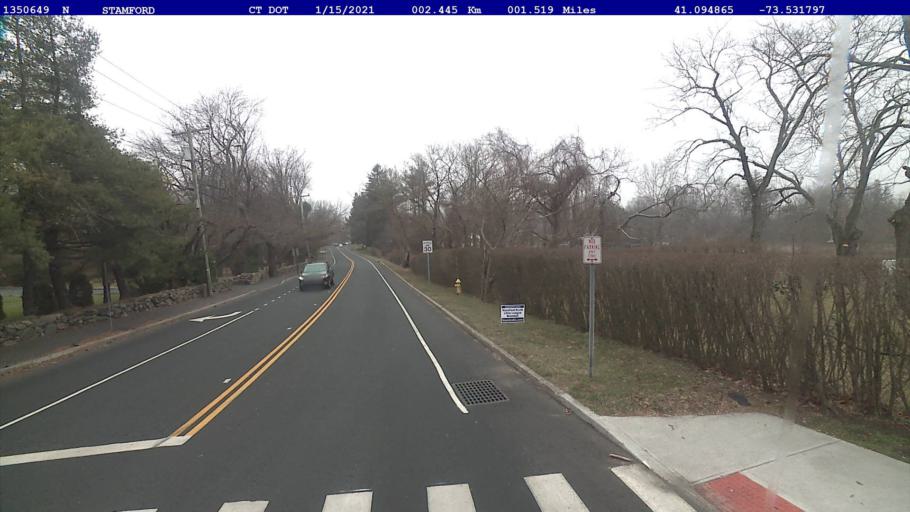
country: US
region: Connecticut
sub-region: Fairfield County
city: Stamford
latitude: 41.0949
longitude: -73.5318
